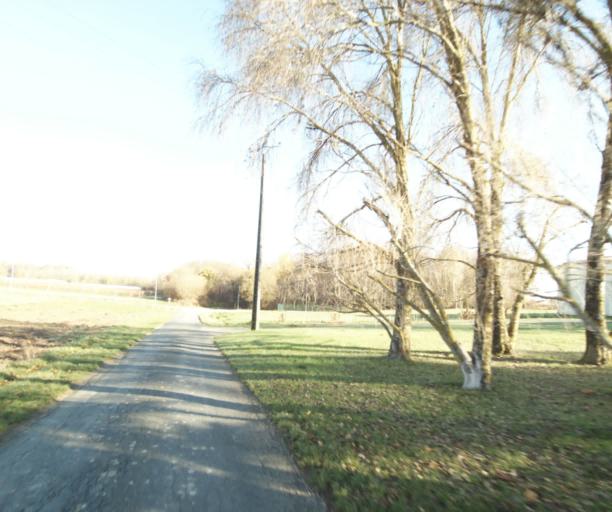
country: FR
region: Poitou-Charentes
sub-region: Departement de la Charente-Maritime
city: Cherac
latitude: 45.7344
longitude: -0.4236
